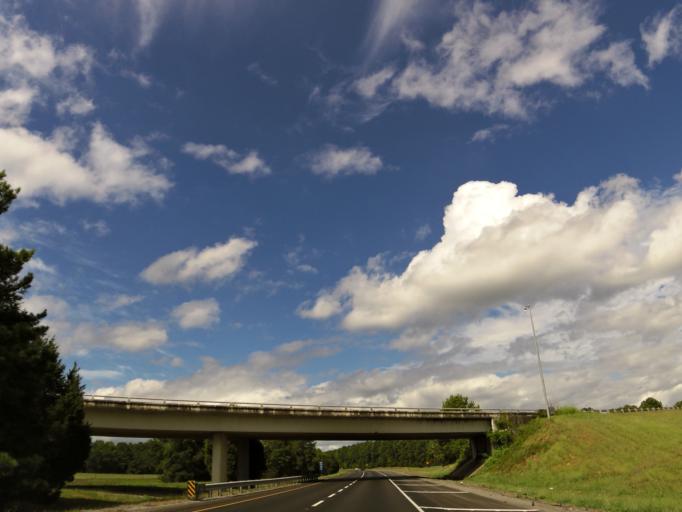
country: US
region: Tennessee
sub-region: Bradley County
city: Hopewell
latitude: 35.3250
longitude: -84.7818
